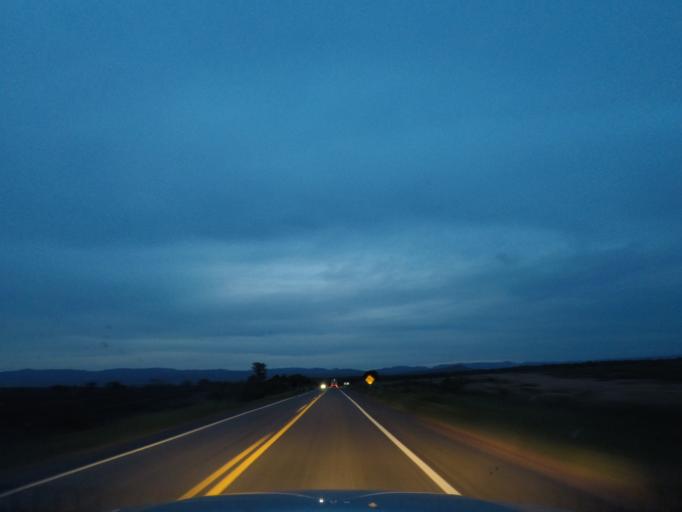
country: BR
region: Bahia
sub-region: Andarai
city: Vera Cruz
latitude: -12.4958
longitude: -41.3000
